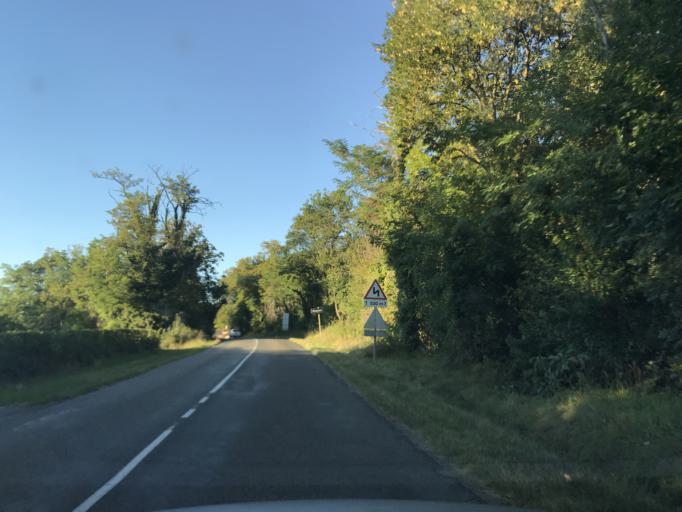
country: FR
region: Aquitaine
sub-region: Departement de la Gironde
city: Lussac
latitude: 44.9424
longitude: -0.0720
